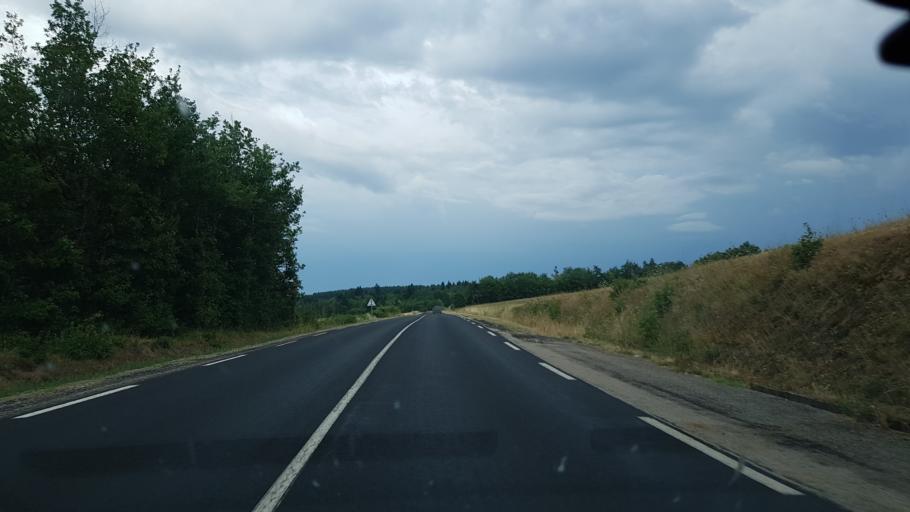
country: FR
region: Auvergne
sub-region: Departement de la Haute-Loire
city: Bournoncle-Saint-Pierre
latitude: 45.2747
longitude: 3.3167
